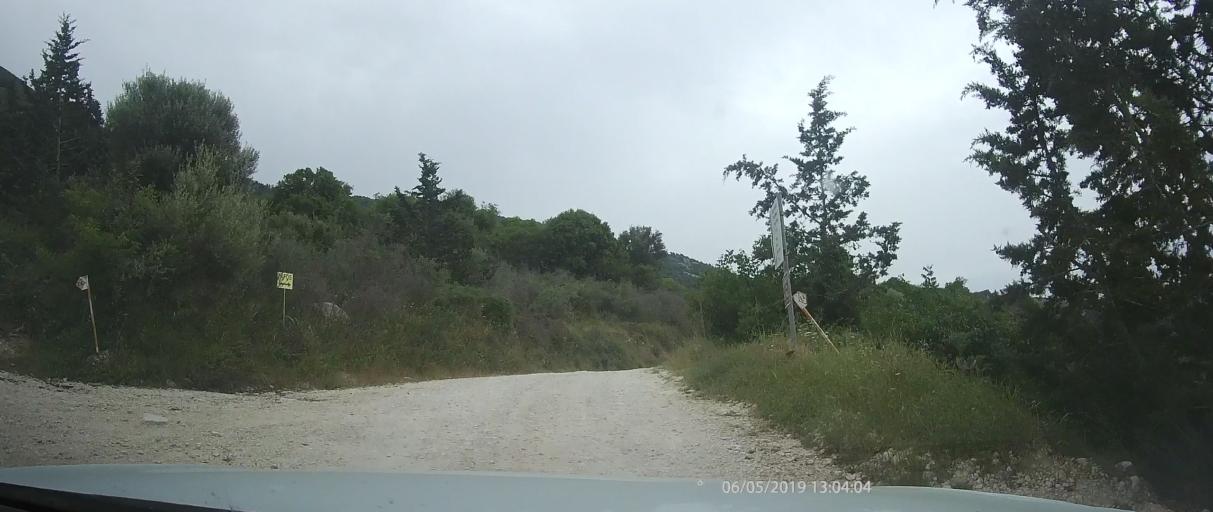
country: CY
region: Pafos
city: Tala
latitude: 34.8664
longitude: 32.4332
